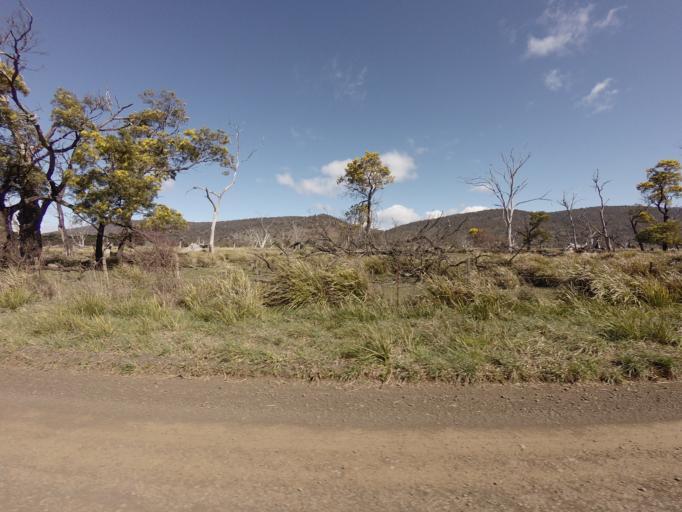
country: AU
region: Tasmania
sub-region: Northern Midlands
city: Evandale
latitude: -41.9476
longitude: 147.4327
